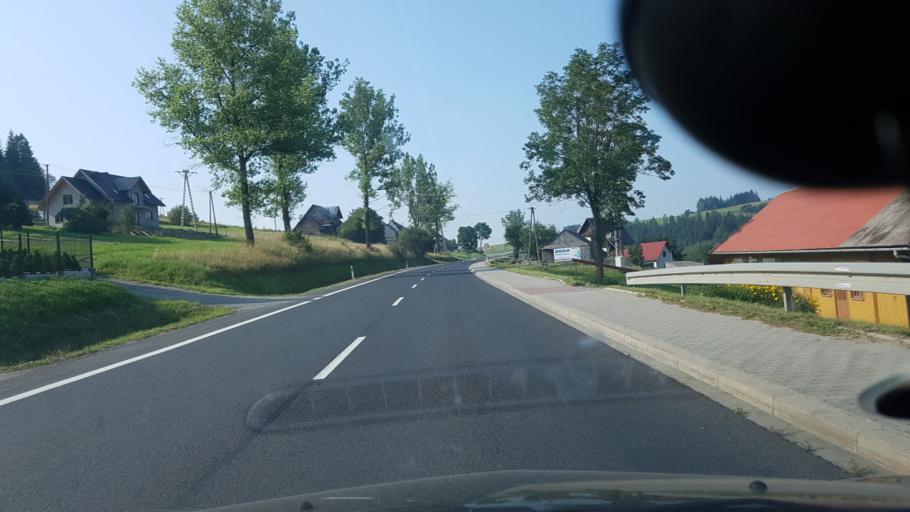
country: PL
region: Lesser Poland Voivodeship
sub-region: Powiat nowotarski
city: Podwilk
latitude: 49.5307
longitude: 19.7142
